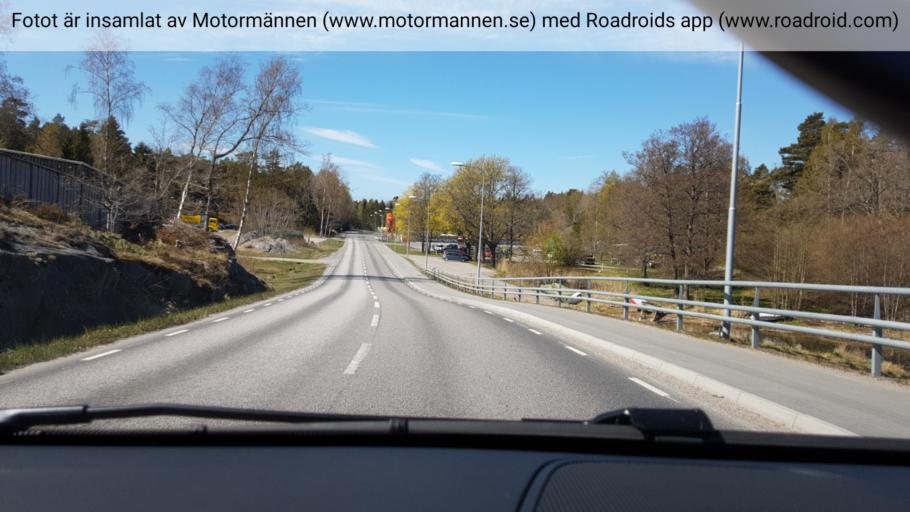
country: SE
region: Stockholm
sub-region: Varmdo Kommun
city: Holo
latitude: 59.2916
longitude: 18.6717
